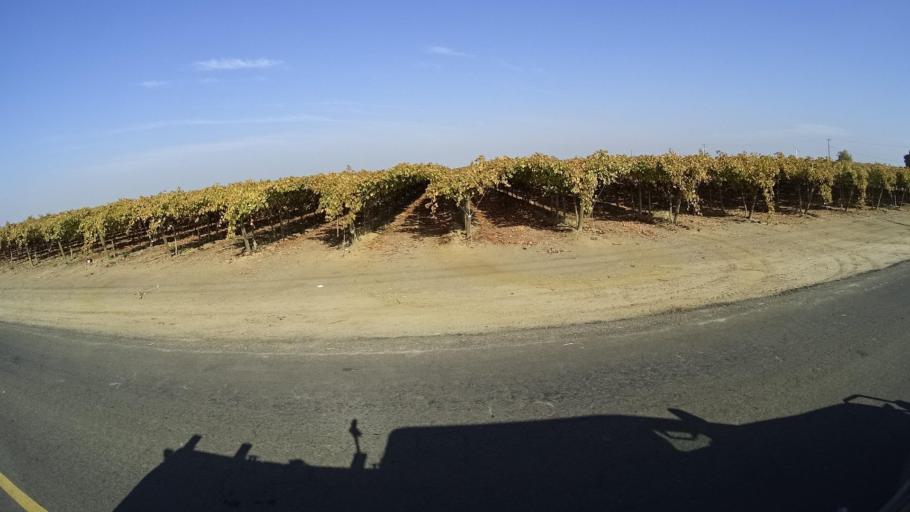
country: US
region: California
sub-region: Kern County
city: McFarland
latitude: 35.6892
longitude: -119.1798
